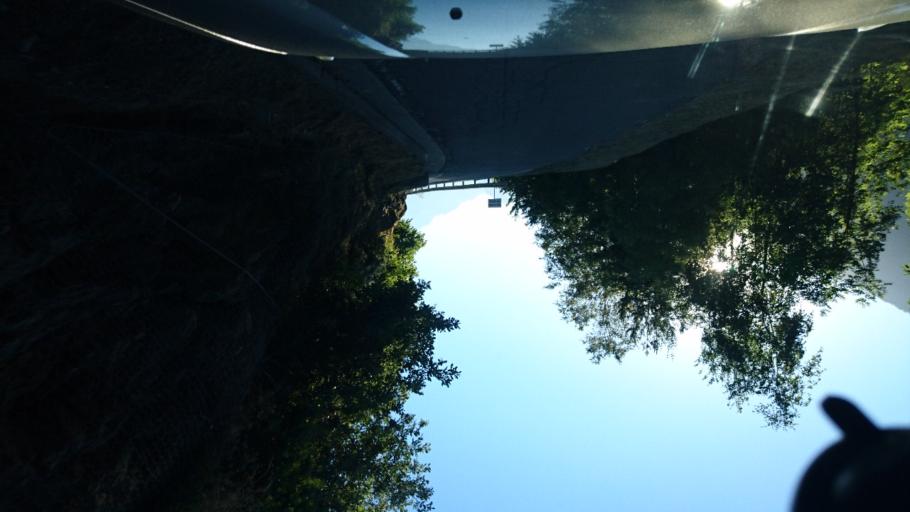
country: IT
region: Aosta Valley
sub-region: Valle d'Aosta
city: Avise
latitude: 45.7132
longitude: 7.1245
